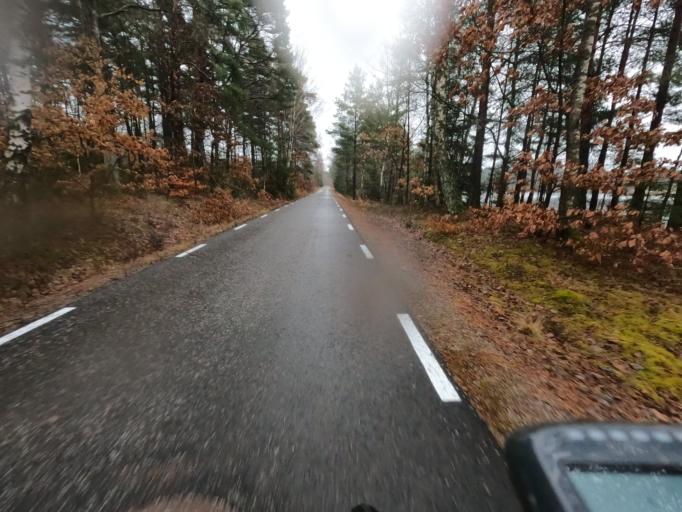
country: SE
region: Halland
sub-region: Halmstads Kommun
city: Aled
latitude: 56.7076
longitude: 13.0509
